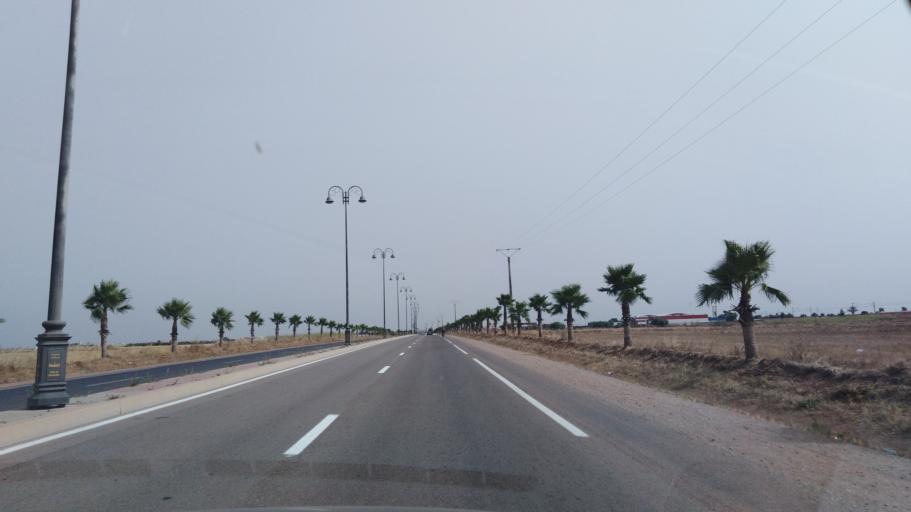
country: MA
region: Chaouia-Ouardigha
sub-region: Settat Province
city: Berrechid
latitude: 33.3030
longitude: -7.5999
